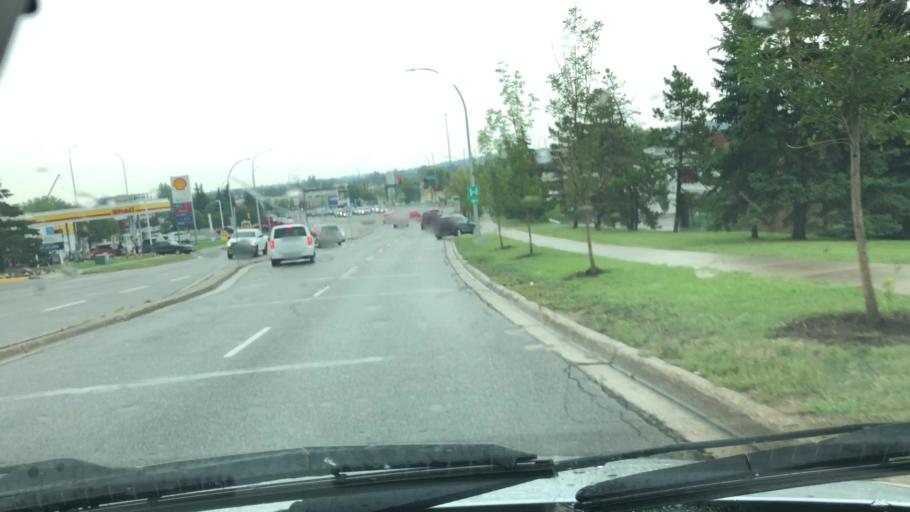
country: CA
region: Alberta
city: St. Albert
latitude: 53.6427
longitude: -113.6285
